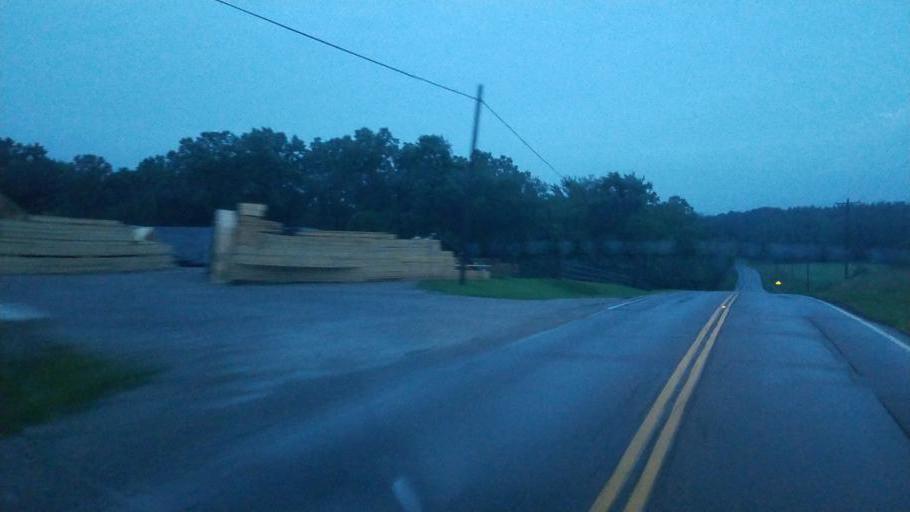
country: US
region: Ohio
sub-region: Knox County
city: Oak Hill
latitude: 40.3340
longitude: -82.2242
